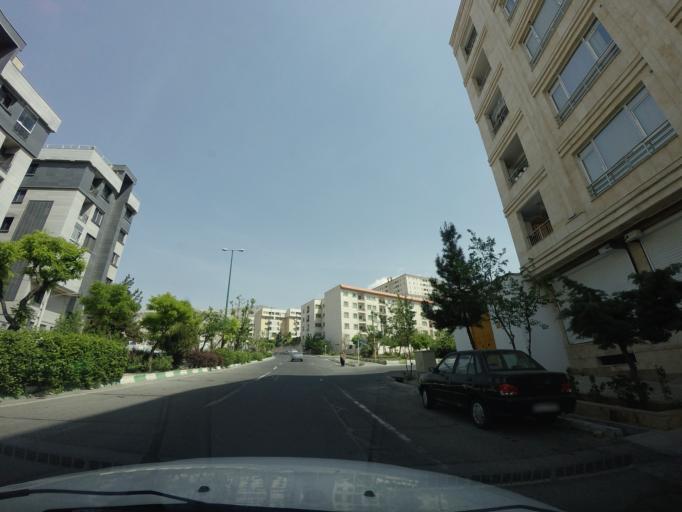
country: IR
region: Tehran
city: Tajrish
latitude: 35.7734
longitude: 51.3269
